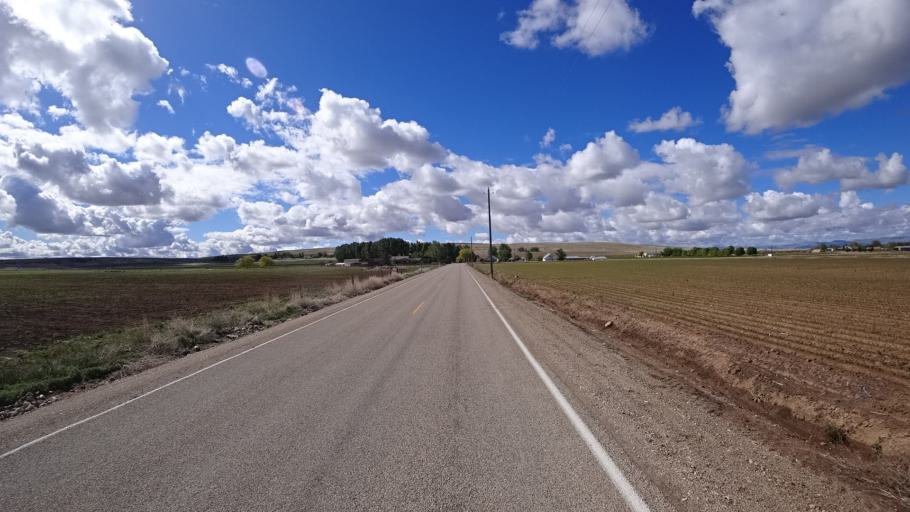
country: US
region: Idaho
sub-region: Ada County
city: Kuna
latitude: 43.4689
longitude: -116.4537
